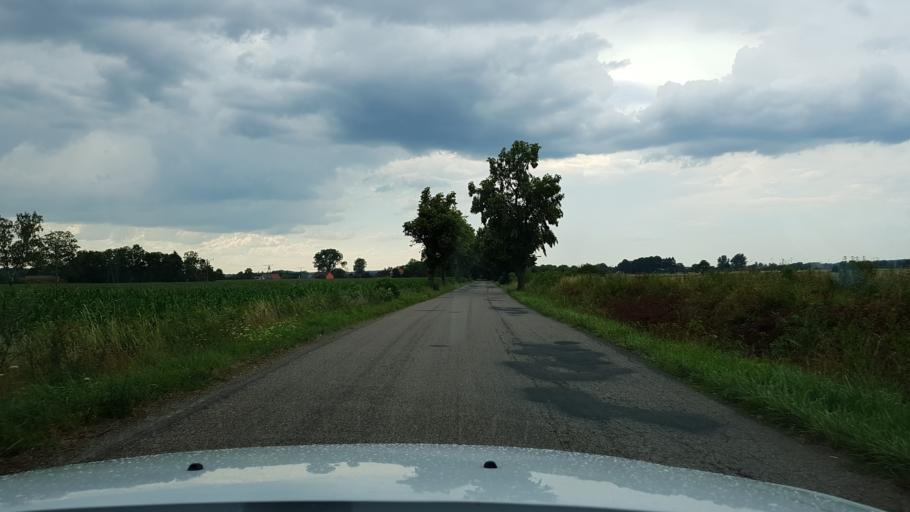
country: PL
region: West Pomeranian Voivodeship
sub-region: Powiat walecki
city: Walcz
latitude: 53.3486
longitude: 16.3725
